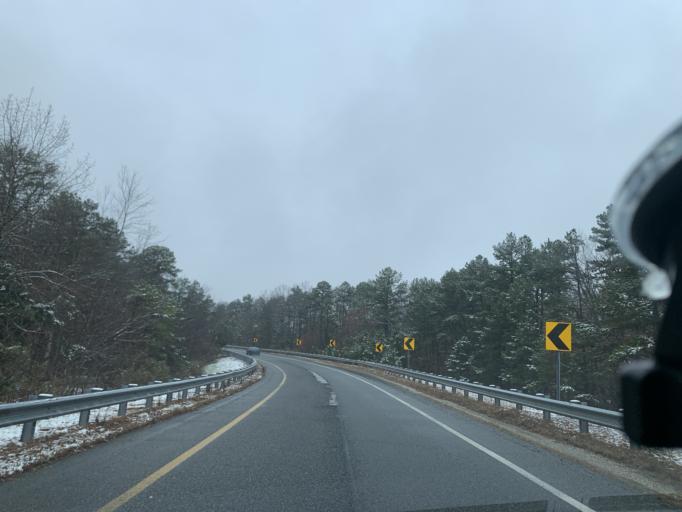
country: US
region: New Jersey
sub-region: Atlantic County
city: Pomona
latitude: 39.4484
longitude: -74.6214
